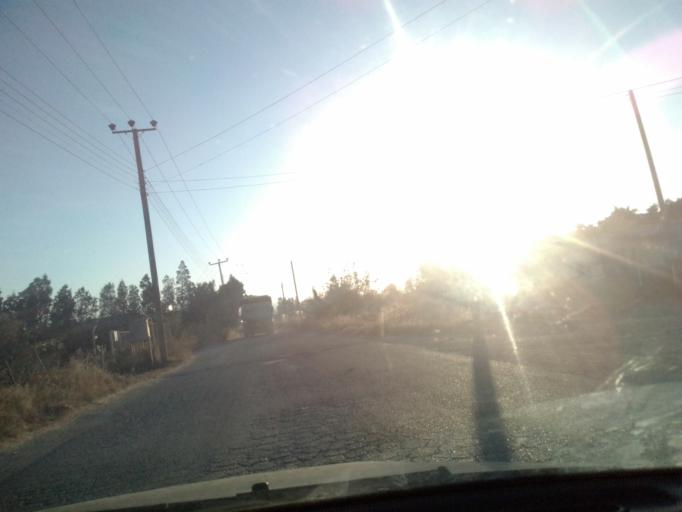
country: CY
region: Limassol
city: Ypsonas
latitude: 34.6794
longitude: 32.9807
